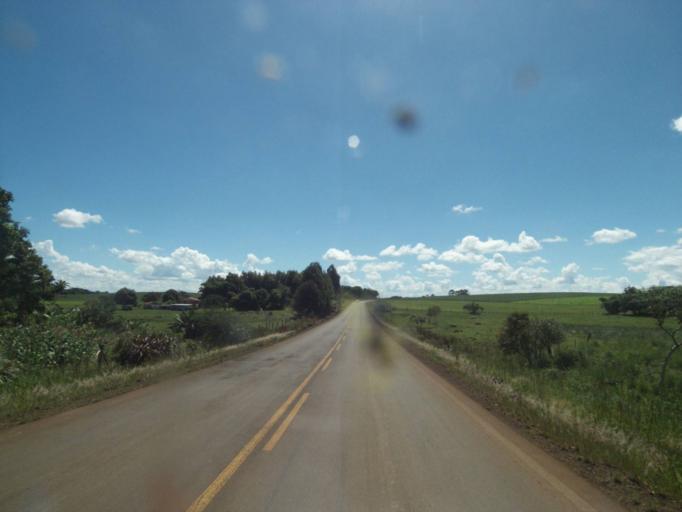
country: BR
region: Parana
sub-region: Pinhao
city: Pinhao
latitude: -25.8131
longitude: -52.0629
